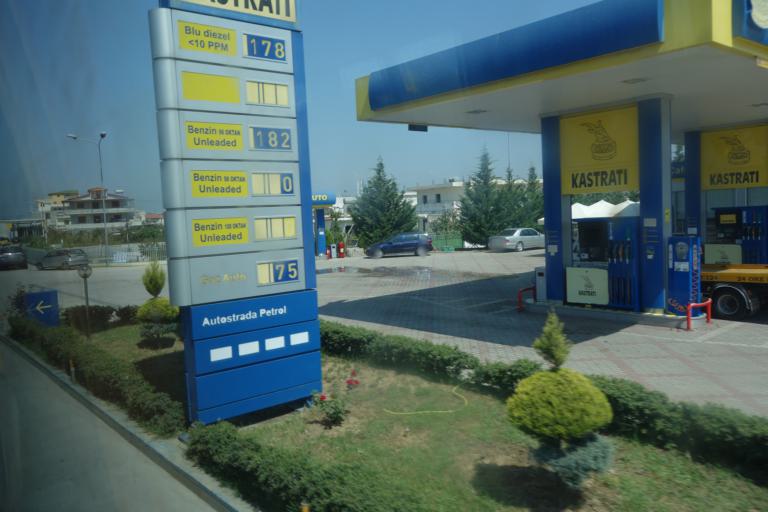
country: AL
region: Durres
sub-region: Rrethi i Durresit
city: Rrashbull
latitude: 41.3343
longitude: 19.4808
